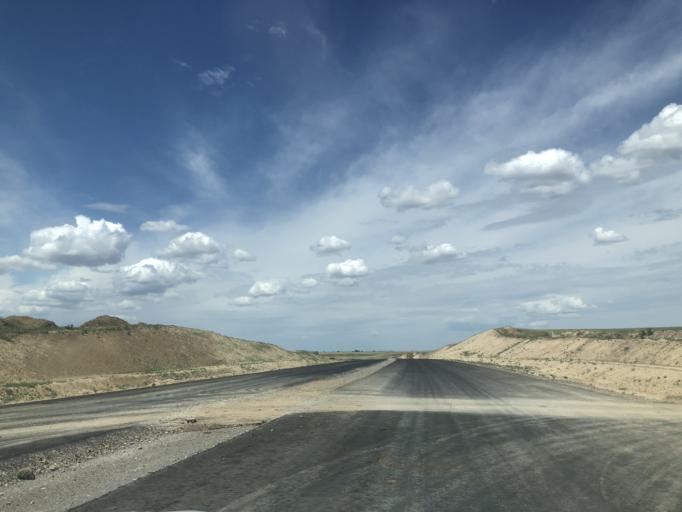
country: KG
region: Chuy
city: Bystrovka
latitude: 43.3171
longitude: 76.0750
